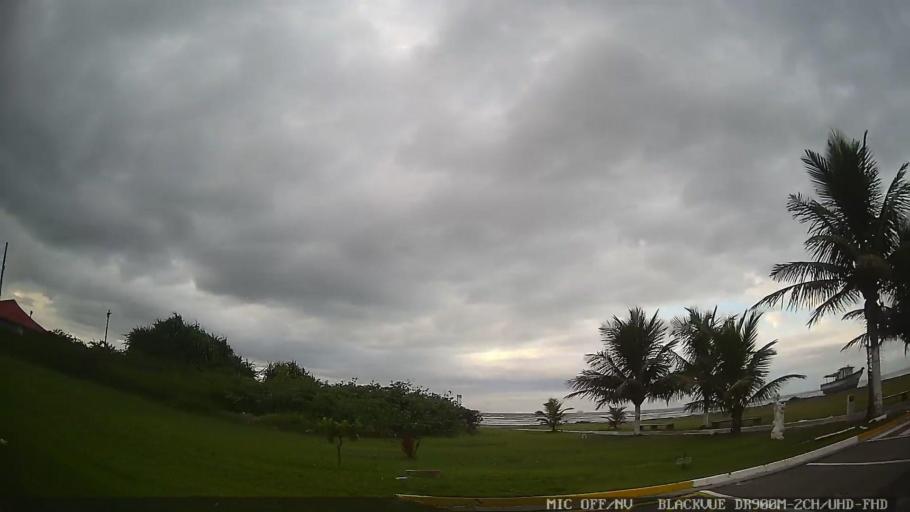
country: BR
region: Sao Paulo
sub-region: Itanhaem
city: Itanhaem
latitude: -24.2332
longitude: -46.8711
